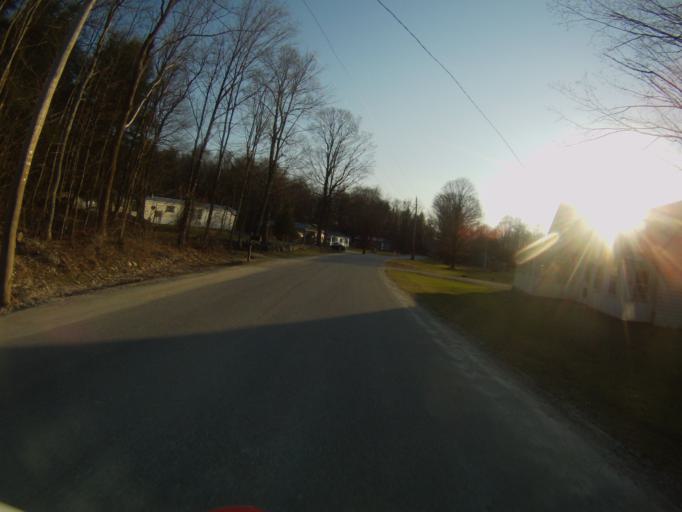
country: US
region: Vermont
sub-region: Addison County
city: Bristol
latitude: 44.0802
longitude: -73.0822
